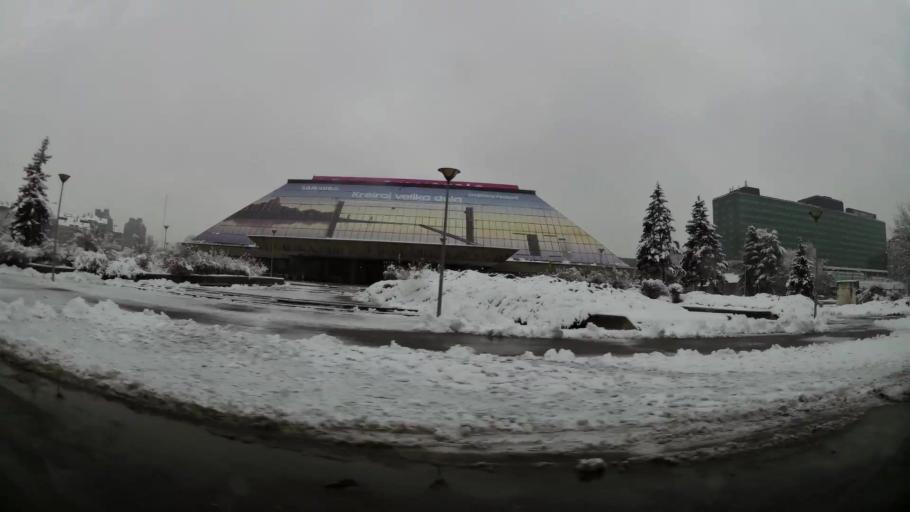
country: RS
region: Central Serbia
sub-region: Belgrade
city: Novi Beograd
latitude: 44.8075
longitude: 20.4344
